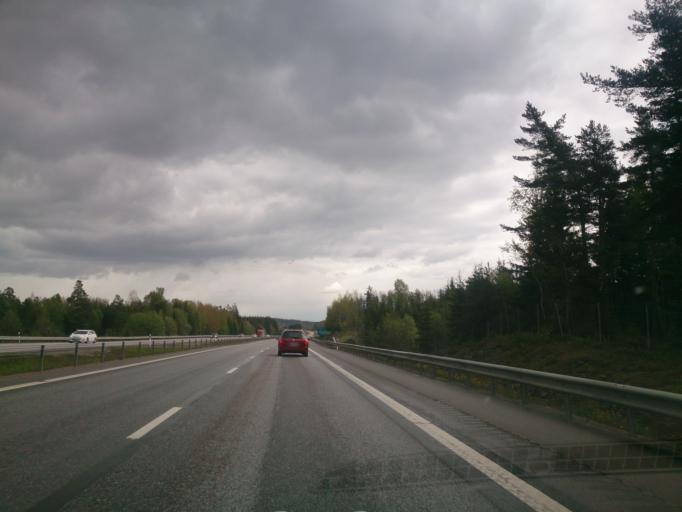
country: SE
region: Soedermanland
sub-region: Trosa Kommun
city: Vagnharad
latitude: 58.9588
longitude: 17.4580
